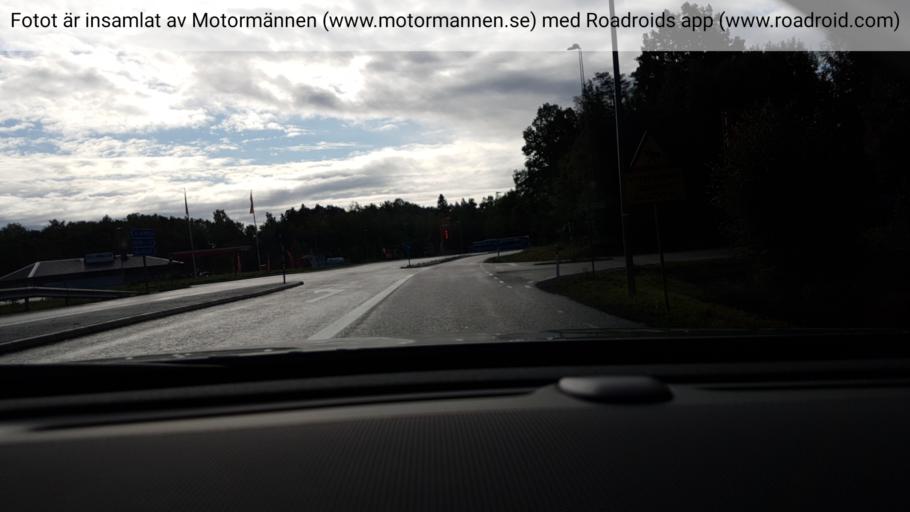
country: SE
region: Vaestra Goetaland
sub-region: Harryda Kommun
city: Ravlanda
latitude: 57.6202
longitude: 12.4332
